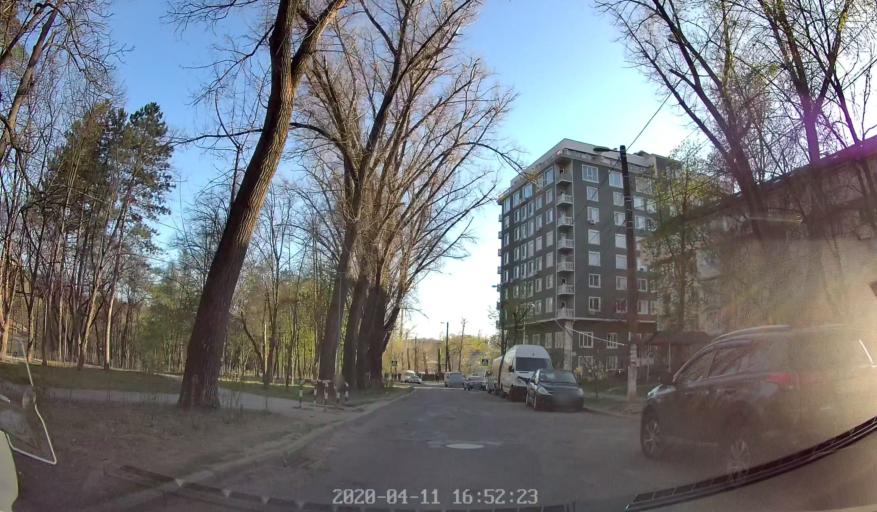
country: MD
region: Chisinau
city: Chisinau
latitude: 47.0395
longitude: 28.8692
